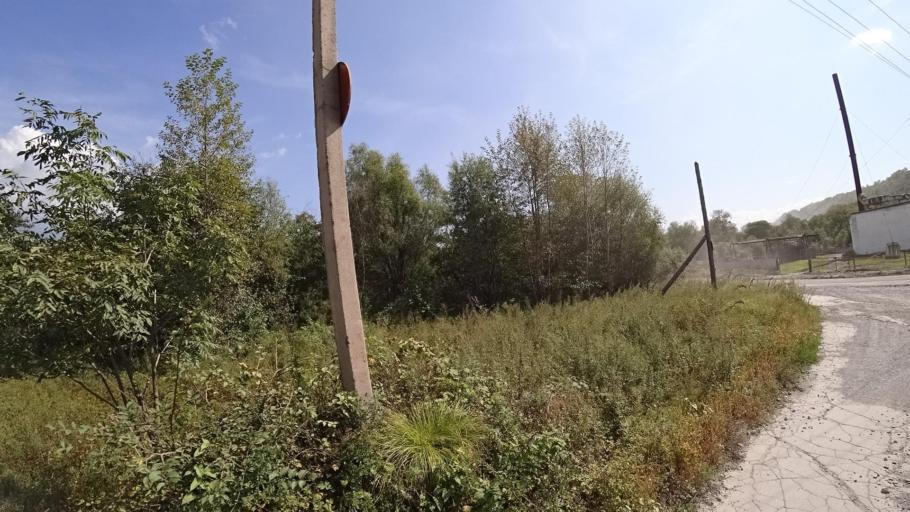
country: RU
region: Jewish Autonomous Oblast
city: Londoko
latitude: 49.0239
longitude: 131.9262
